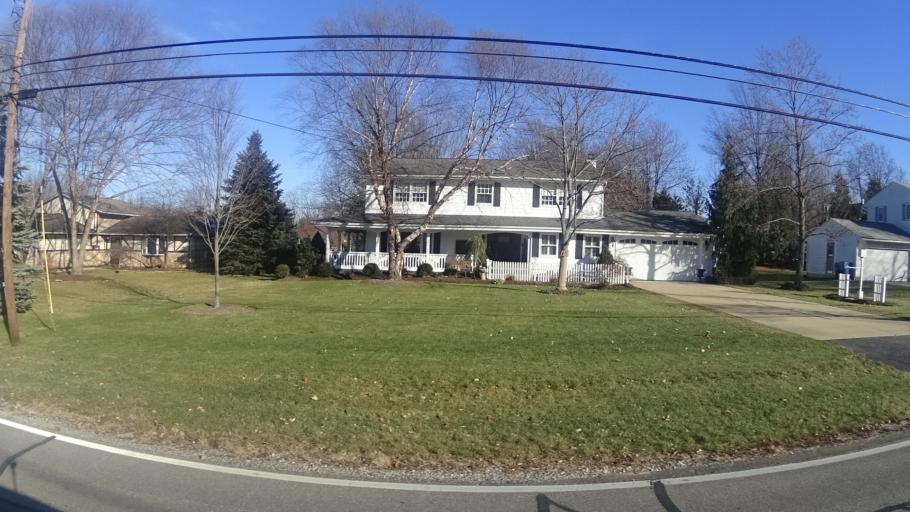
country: US
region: Ohio
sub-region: Lorain County
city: Vermilion
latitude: 41.4060
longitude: -82.3420
